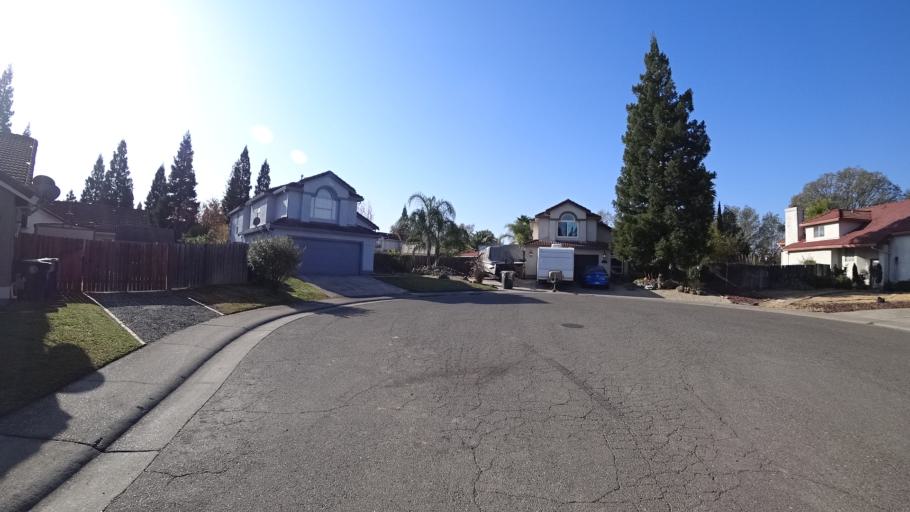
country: US
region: California
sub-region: Sacramento County
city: Citrus Heights
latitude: 38.7025
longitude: -121.2499
